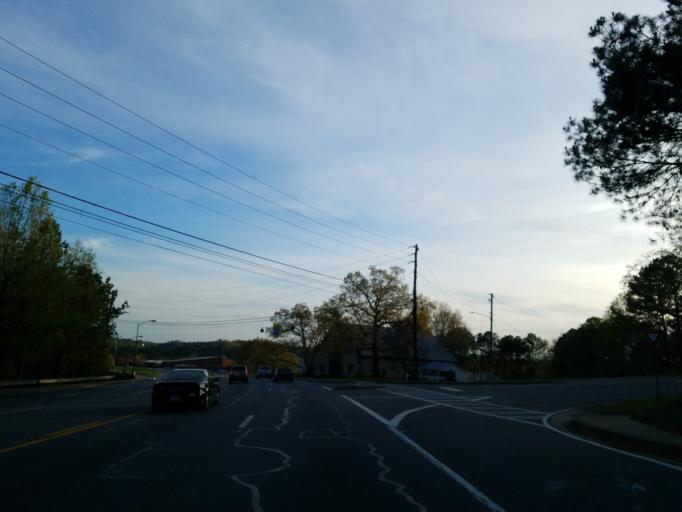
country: US
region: Georgia
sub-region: Cherokee County
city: Canton
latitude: 34.2386
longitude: -84.4992
